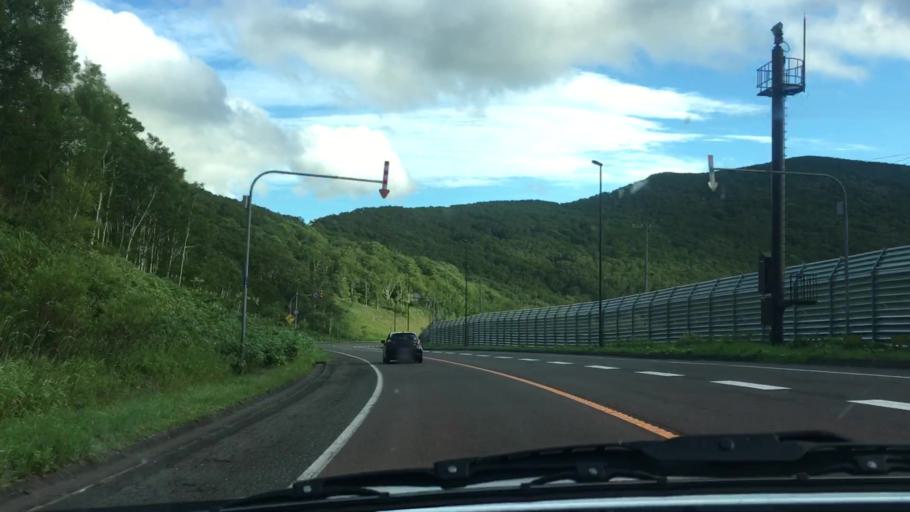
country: JP
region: Hokkaido
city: Shimo-furano
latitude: 43.1322
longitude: 142.7622
